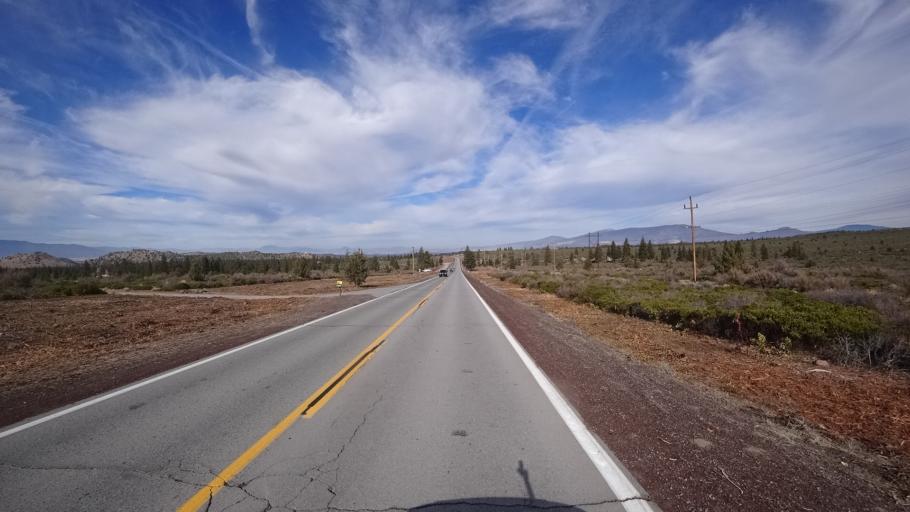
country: US
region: California
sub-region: Siskiyou County
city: Weed
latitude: 41.4855
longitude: -122.3623
